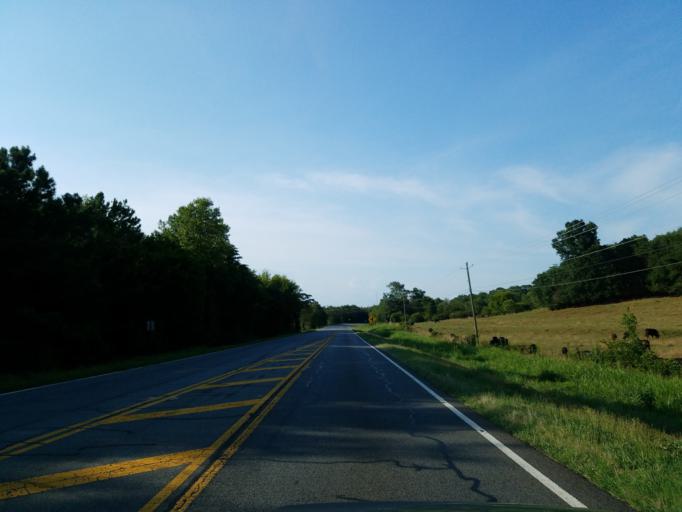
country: US
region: Georgia
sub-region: Bartow County
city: Rydal
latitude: 34.3783
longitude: -84.7094
